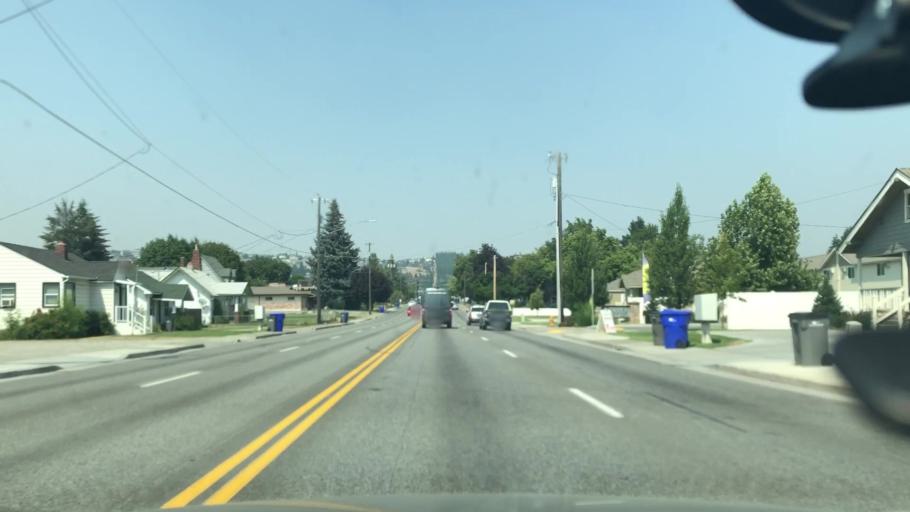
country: US
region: Washington
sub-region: Spokane County
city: Millwood
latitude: 47.6928
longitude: -117.2828
